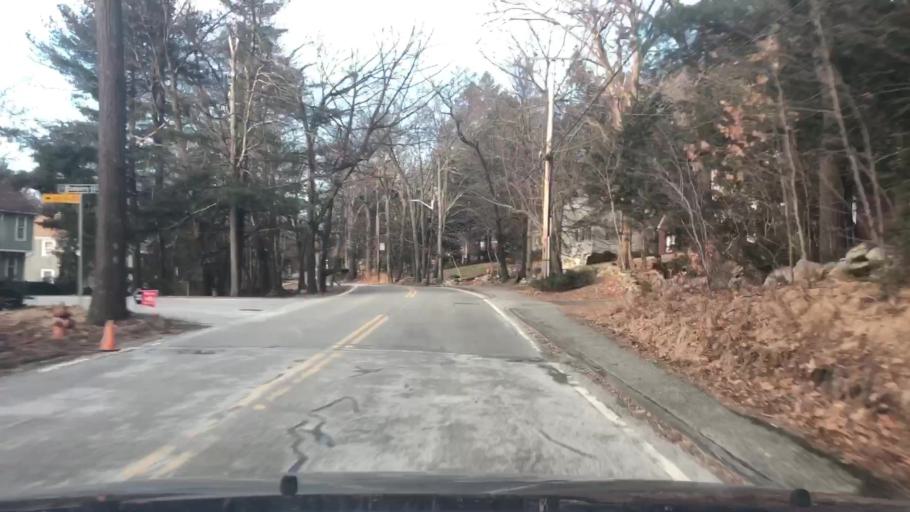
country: US
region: Massachusetts
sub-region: Essex County
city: Andover
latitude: 42.6699
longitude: -71.1106
